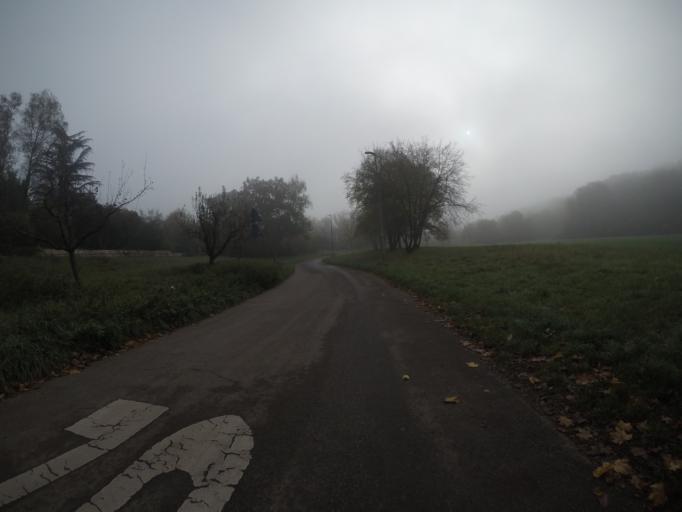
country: DE
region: Baden-Wuerttemberg
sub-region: Regierungsbezirk Stuttgart
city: Neuhausen auf den Fildern
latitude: 48.7065
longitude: 9.2703
